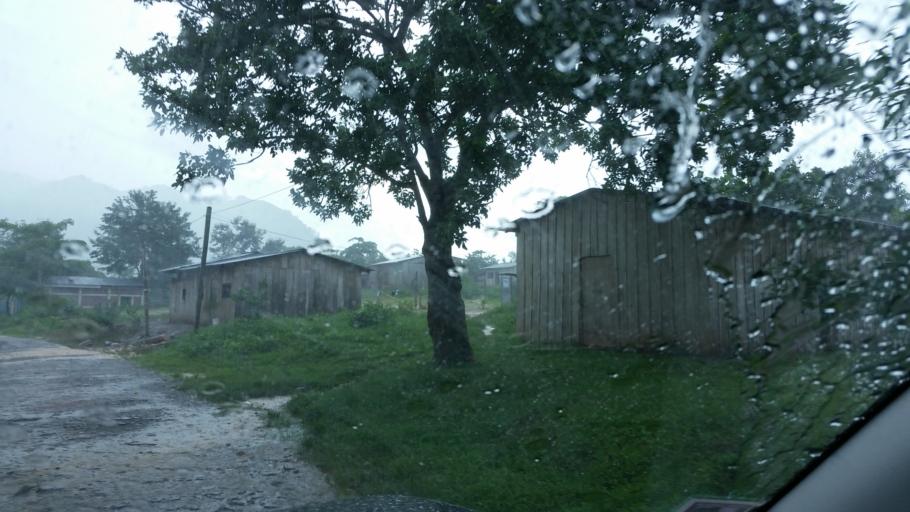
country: NI
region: Atlantico Norte (RAAN)
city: Waslala
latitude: 13.1562
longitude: -85.4374
